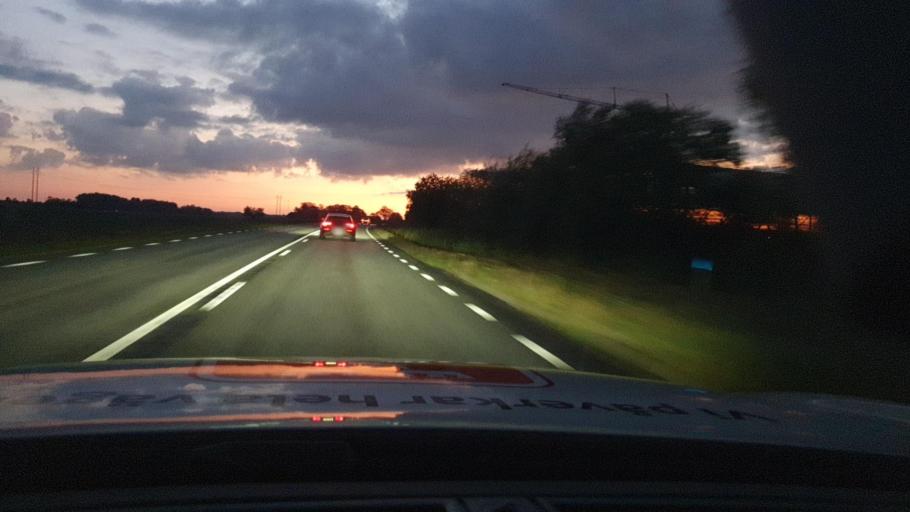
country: SE
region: Skane
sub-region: Angelholms Kommun
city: AEngelholm
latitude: 56.2261
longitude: 12.8692
